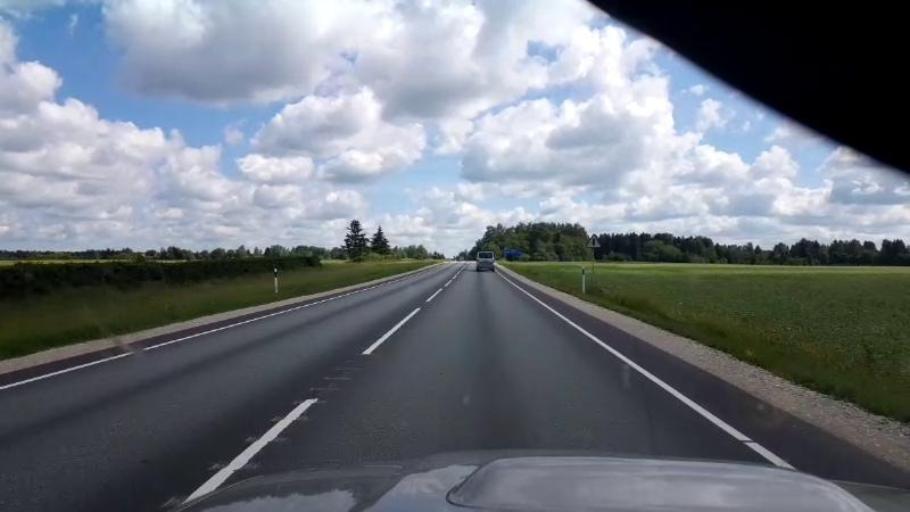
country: EE
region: Laeaene-Virumaa
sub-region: Tapa vald
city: Tapa
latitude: 59.2625
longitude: 26.0123
